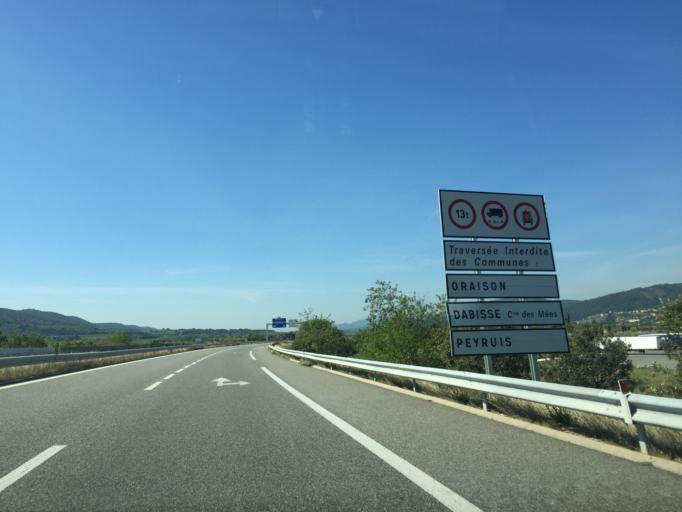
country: FR
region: Provence-Alpes-Cote d'Azur
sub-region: Departement des Alpes-de-Haute-Provence
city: Les Mees
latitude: 44.0451
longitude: 5.9700
